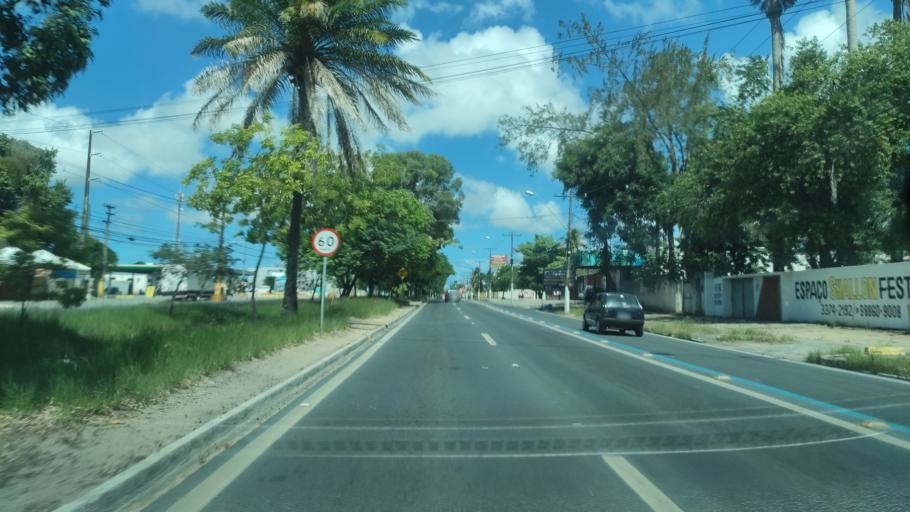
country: BR
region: Alagoas
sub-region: Satuba
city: Satuba
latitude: -9.5826
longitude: -35.7660
